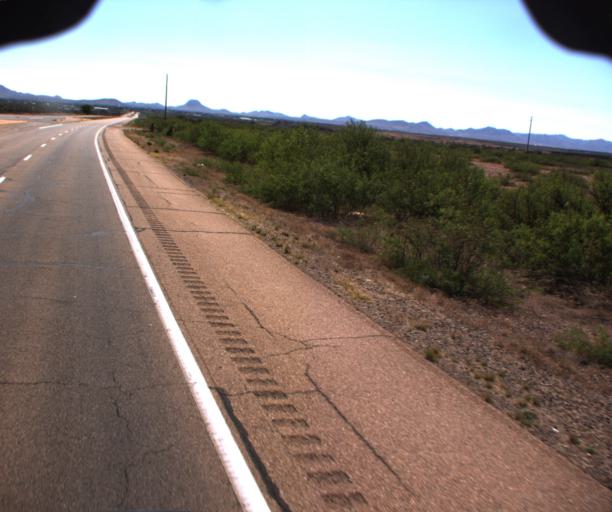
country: US
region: Arizona
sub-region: Cochise County
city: Pirtleville
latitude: 31.3541
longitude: -109.5980
